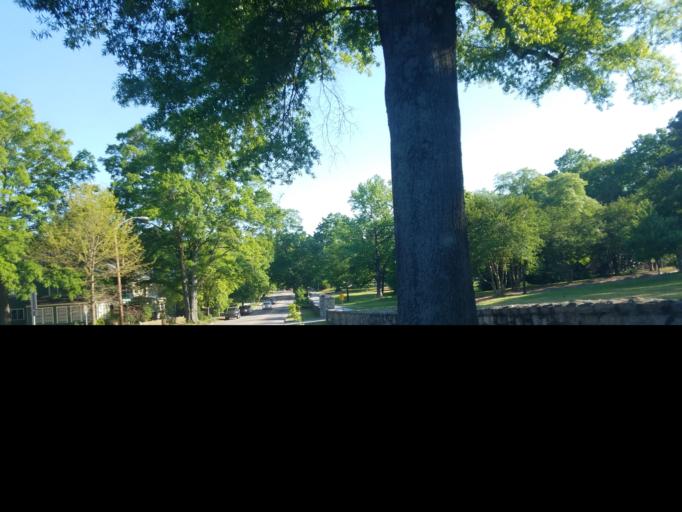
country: US
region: North Carolina
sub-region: Durham County
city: Durham
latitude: 36.0081
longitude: -78.9123
